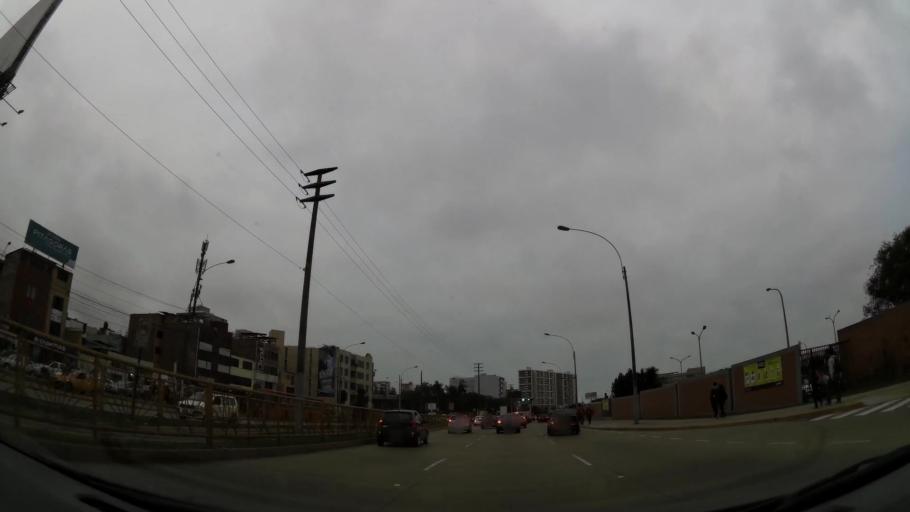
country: PE
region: Callao
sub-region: Callao
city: Callao
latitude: -12.0693
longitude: -77.0780
